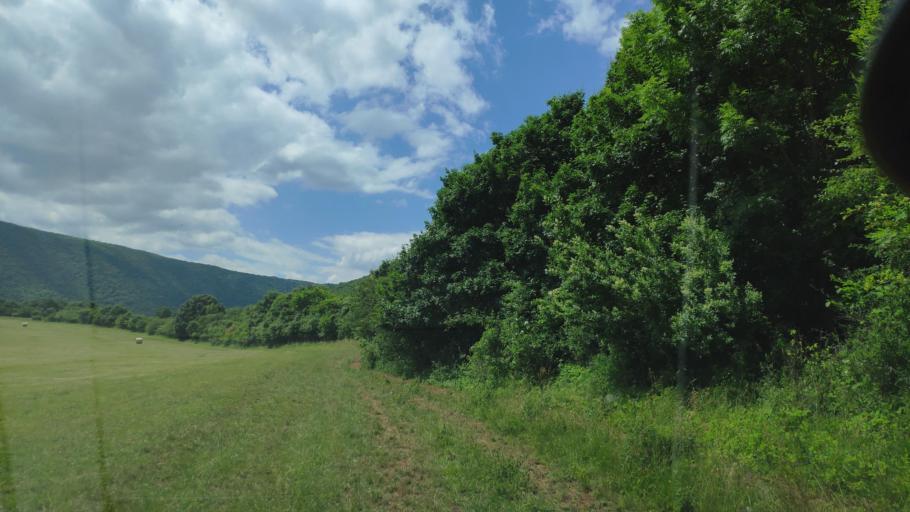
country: SK
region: Kosicky
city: Medzev
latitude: 48.6236
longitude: 20.8840
